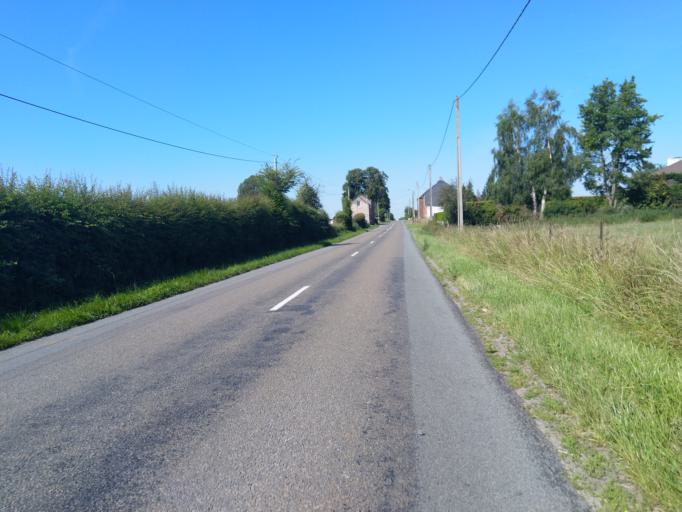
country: FR
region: Nord-Pas-de-Calais
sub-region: Departement du Nord
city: La Longueville
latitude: 50.3145
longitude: 3.8577
